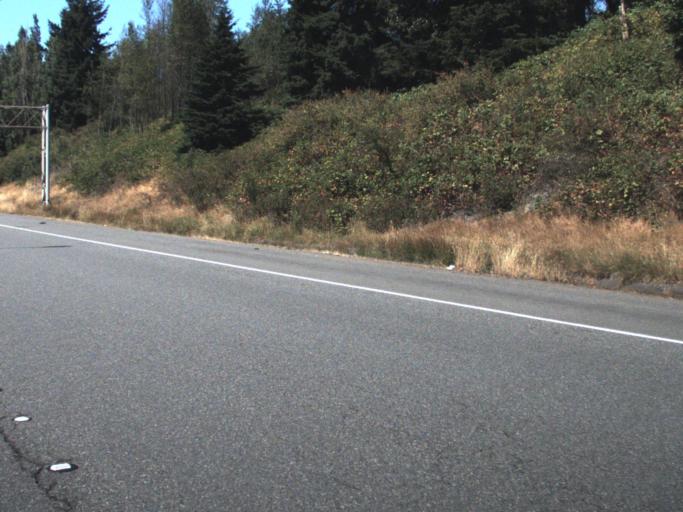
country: US
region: Washington
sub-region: King County
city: Riverton
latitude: 47.4676
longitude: -122.3047
